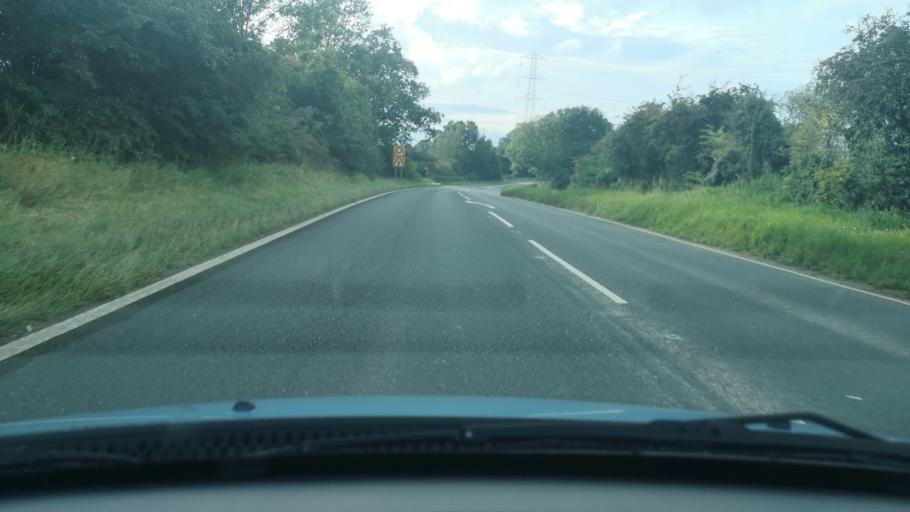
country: GB
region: England
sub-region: Doncaster
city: Marr
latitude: 53.5842
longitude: -1.2339
